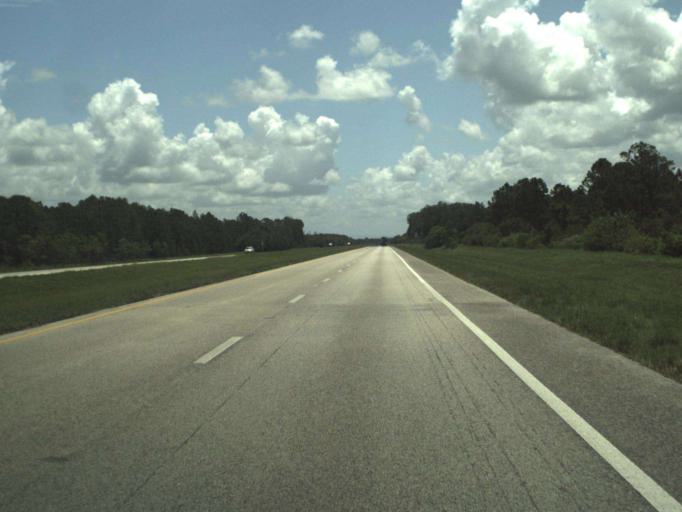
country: US
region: Florida
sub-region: Indian River County
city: Fellsmere
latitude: 27.6814
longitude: -80.8607
